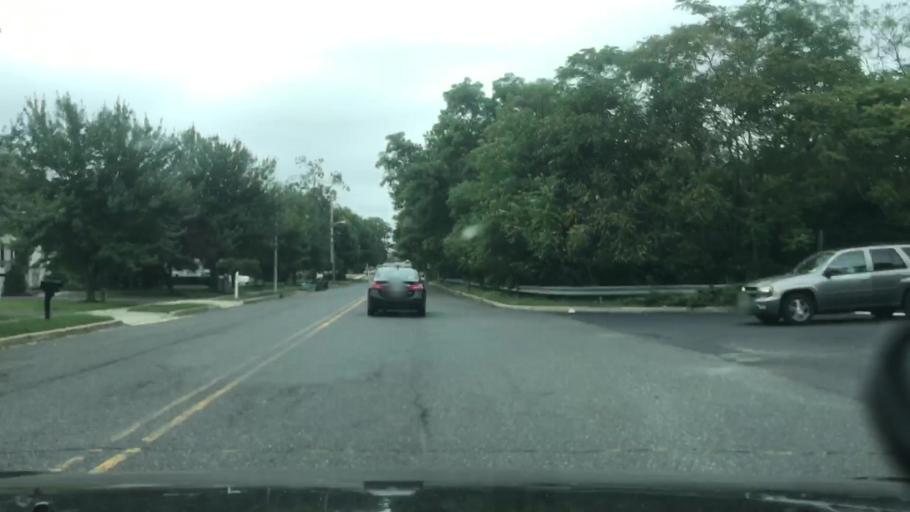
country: US
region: New Jersey
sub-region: Monmouth County
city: Eatontown
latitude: 40.2891
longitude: -74.0439
